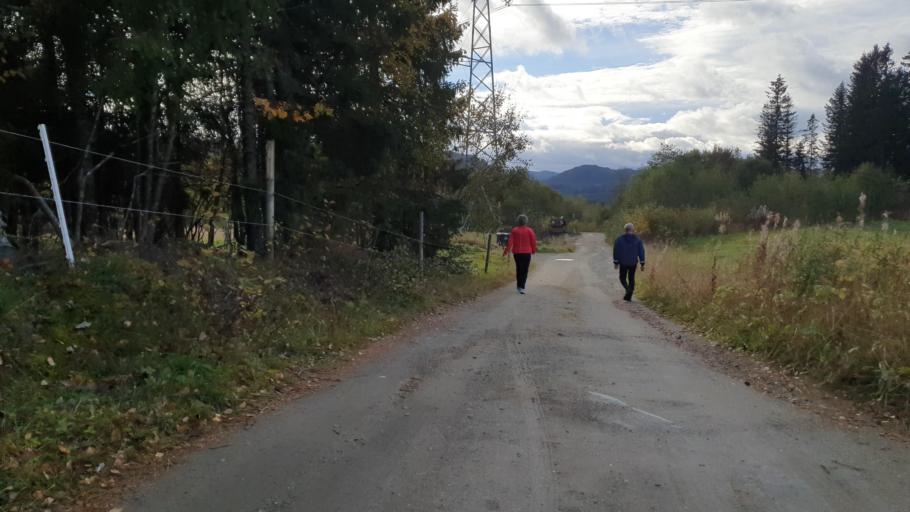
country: NO
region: Sor-Trondelag
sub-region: Klaebu
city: Klaebu
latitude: 63.2929
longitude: 10.4632
